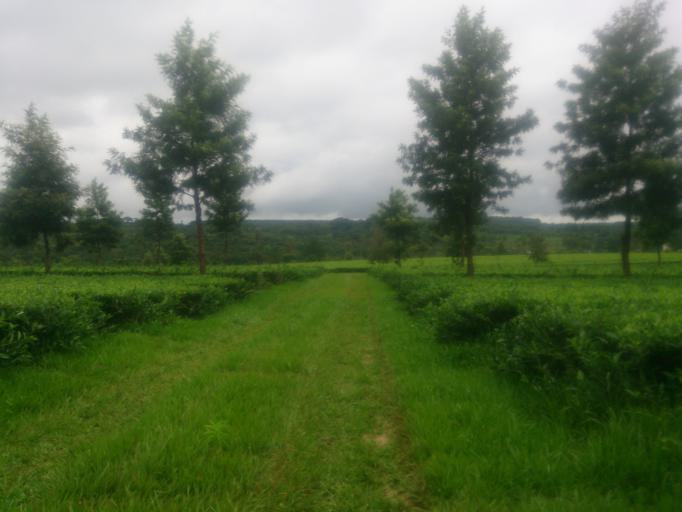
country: AR
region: Misiones
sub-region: Departamento de Obera
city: Obera
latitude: -27.4422
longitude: -55.0856
